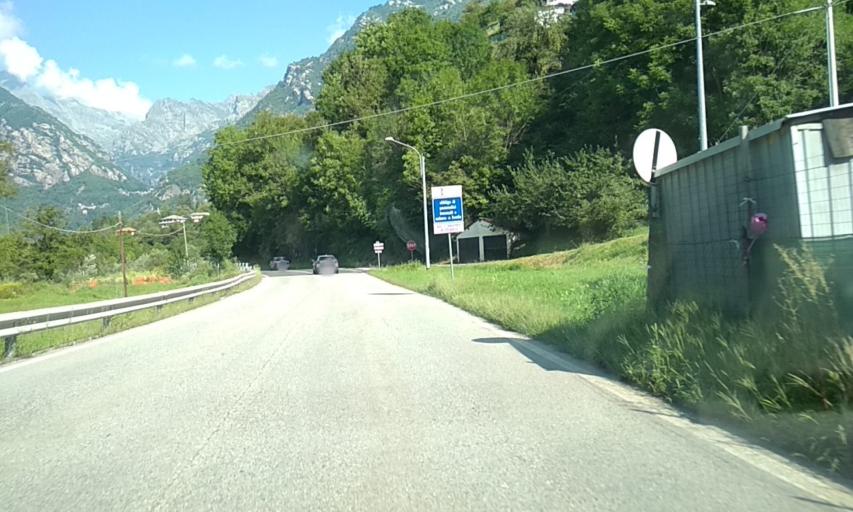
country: IT
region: Piedmont
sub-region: Provincia di Torino
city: Locana
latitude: 45.4213
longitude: 7.4448
